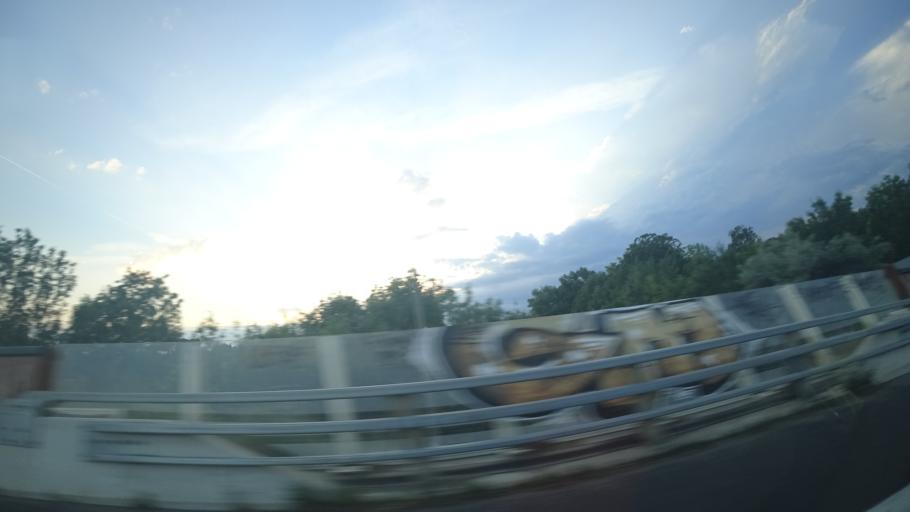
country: FR
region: Languedoc-Roussillon
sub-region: Departement de l'Herault
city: Pezenas
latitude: 43.4716
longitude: 3.4350
